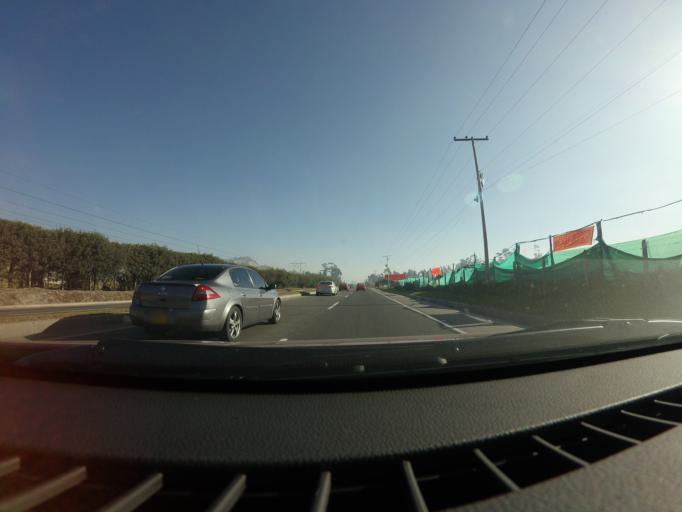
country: CO
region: Cundinamarca
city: Cogua
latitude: 5.0665
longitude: -73.9474
